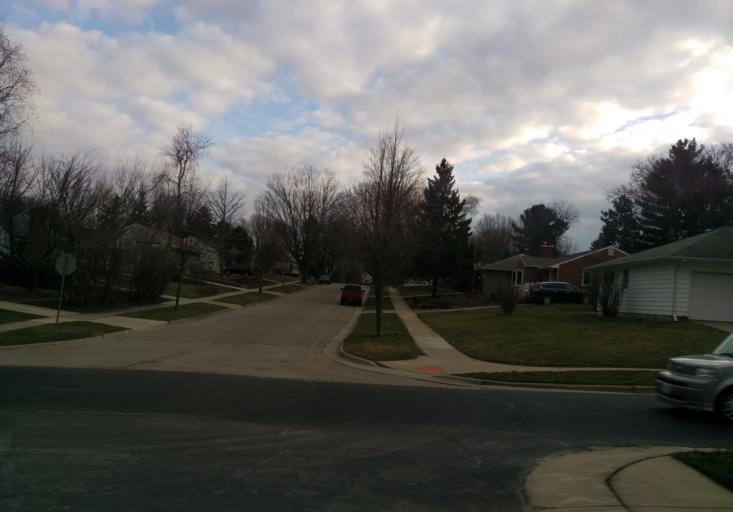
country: US
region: Wisconsin
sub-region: Dane County
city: Shorewood Hills
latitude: 43.0536
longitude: -89.4469
